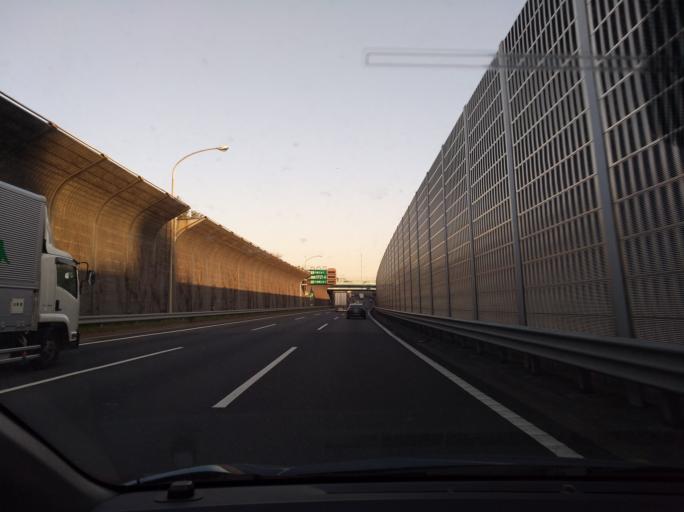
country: JP
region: Chiba
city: Chiba
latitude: 35.6463
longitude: 140.0662
